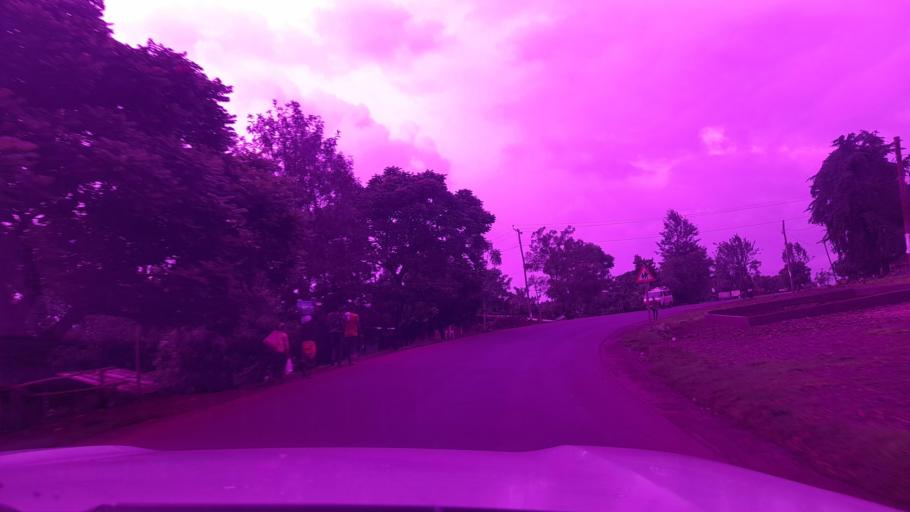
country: ET
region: Oromiya
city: Jima
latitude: 7.9619
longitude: 37.4409
